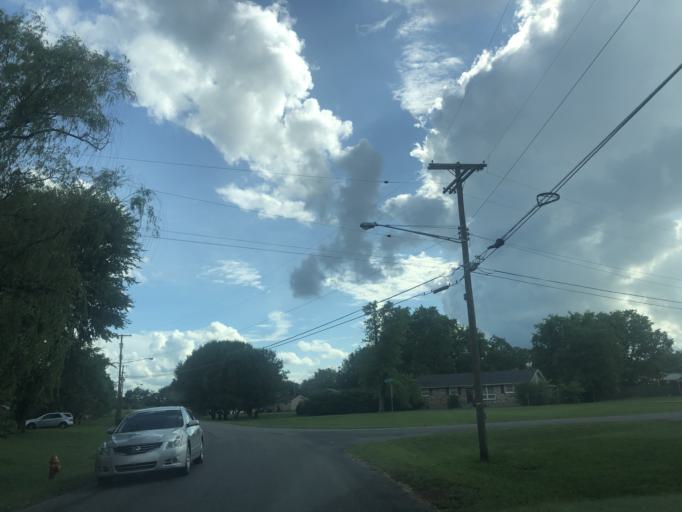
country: US
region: Tennessee
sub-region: Davidson County
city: Nashville
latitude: 36.2087
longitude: -86.8541
